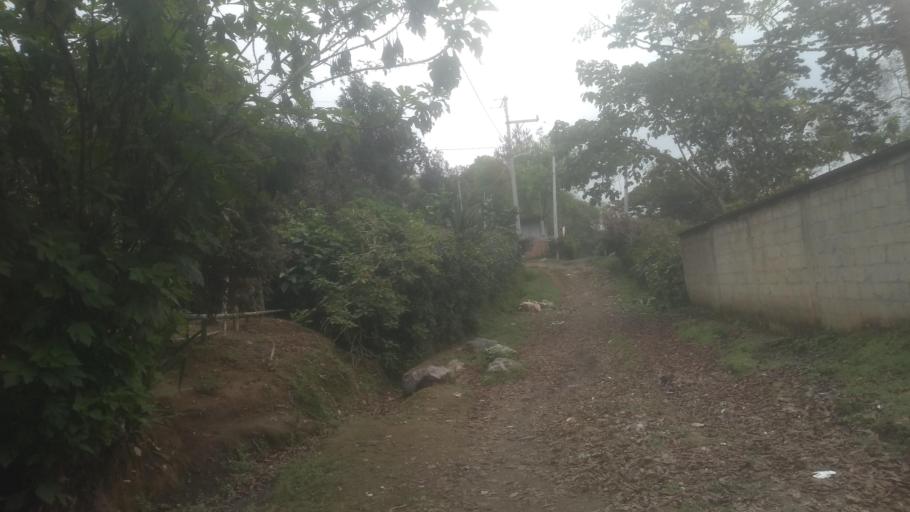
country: MX
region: Veracruz
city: Chocaman
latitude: 18.9892
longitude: -97.0568
